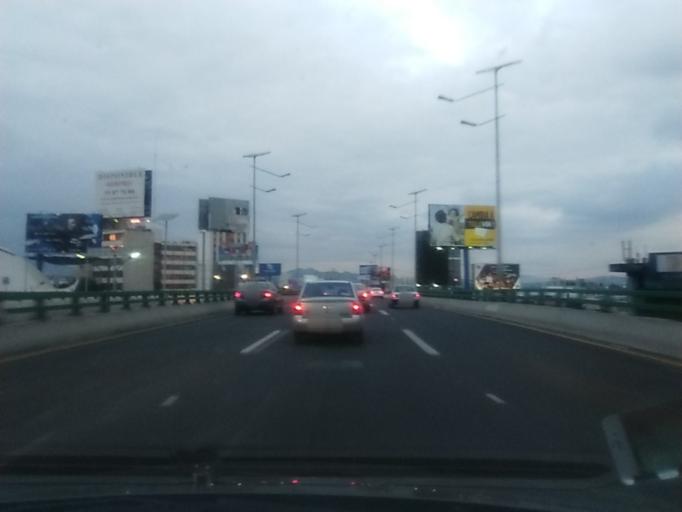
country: MX
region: Mexico
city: Naucalpan de Juarez
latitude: 19.4659
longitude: -99.2246
